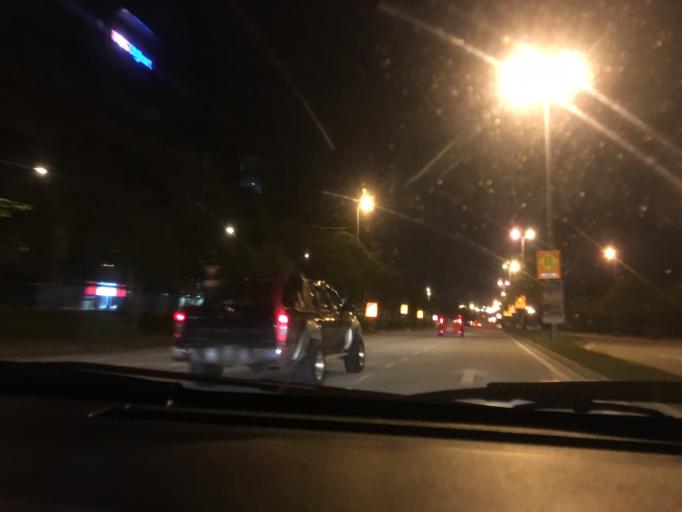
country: MY
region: Putrajaya
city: Putrajaya
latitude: 2.9114
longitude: 101.6514
